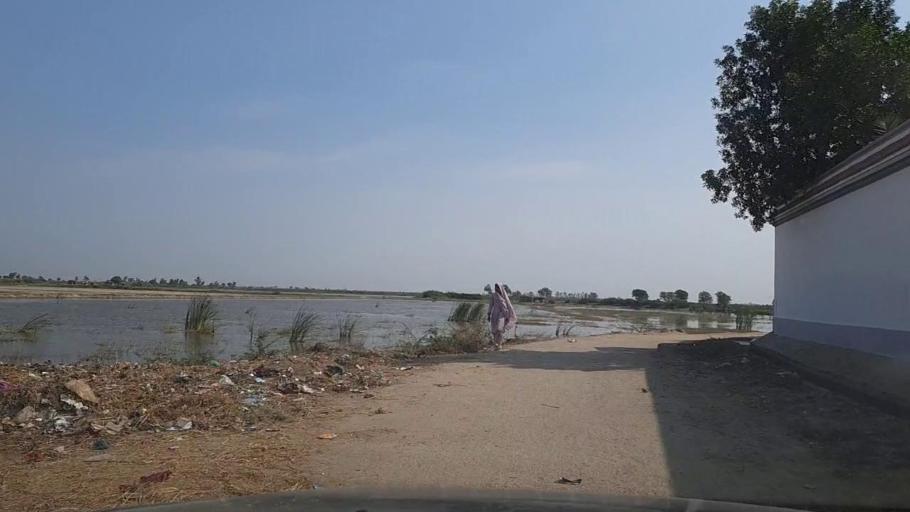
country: PK
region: Sindh
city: Thatta
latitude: 24.5663
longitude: 67.8916
